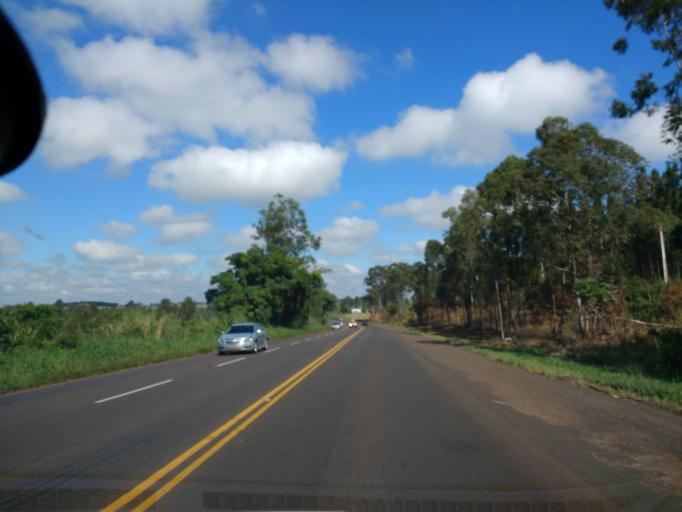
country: BR
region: Parana
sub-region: Cianorte
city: Cianorte
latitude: -23.7071
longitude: -52.6495
